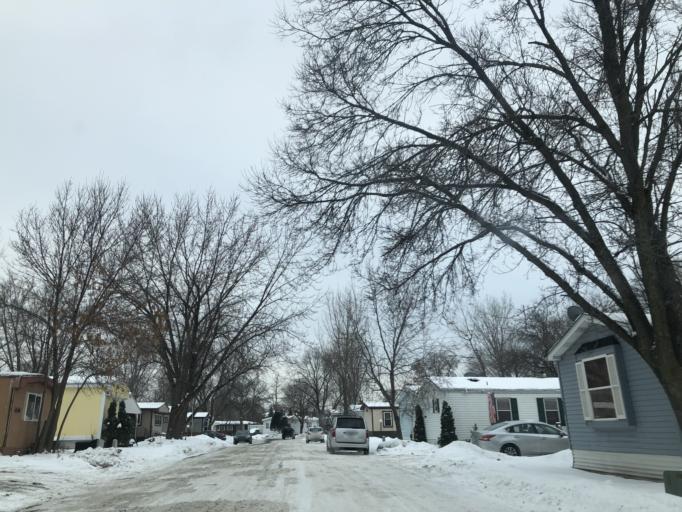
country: US
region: Minnesota
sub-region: Ramsey County
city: New Brighton
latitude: 45.0810
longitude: -93.1829
